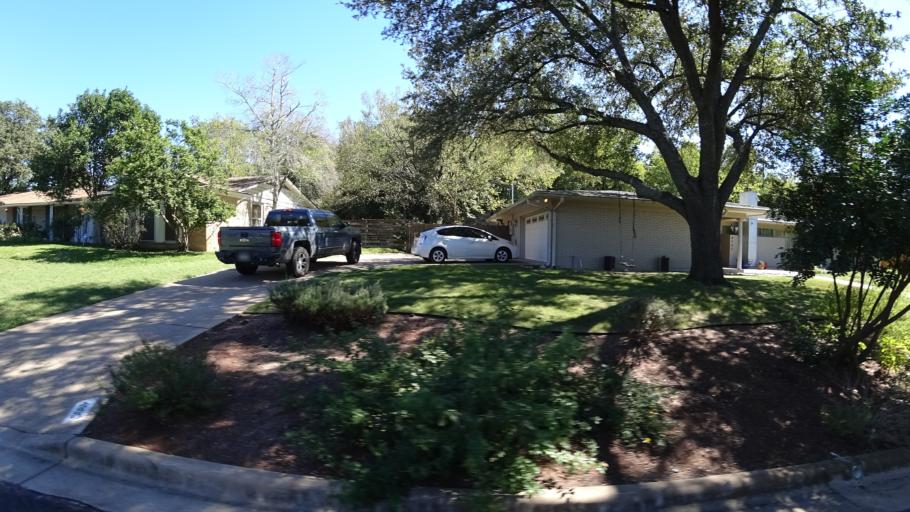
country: US
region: Texas
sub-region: Travis County
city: West Lake Hills
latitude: 30.3354
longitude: -97.7676
